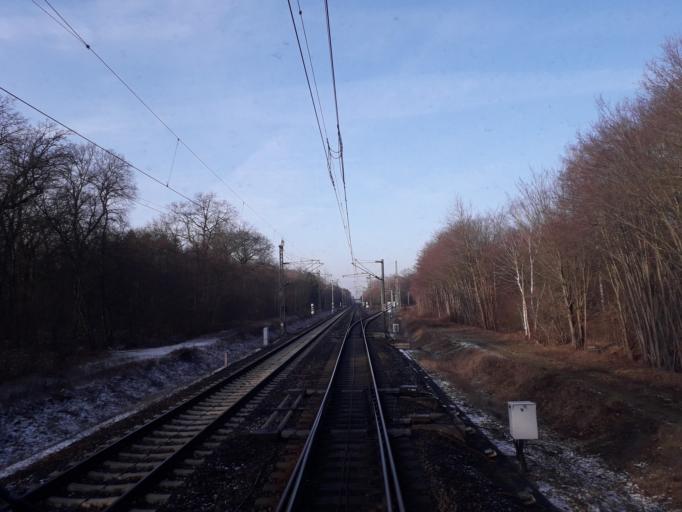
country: DE
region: Brandenburg
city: Brieselang
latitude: 52.5745
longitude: 13.0326
